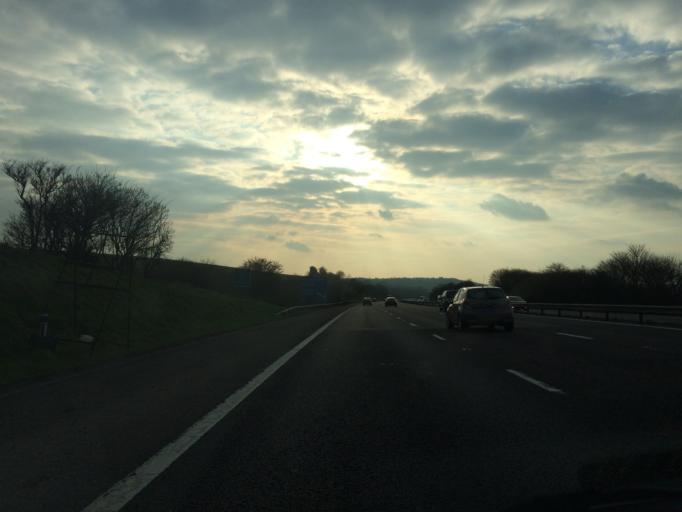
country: GB
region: England
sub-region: Borough of Swindon
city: Wanborough
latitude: 51.5255
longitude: -1.7024
